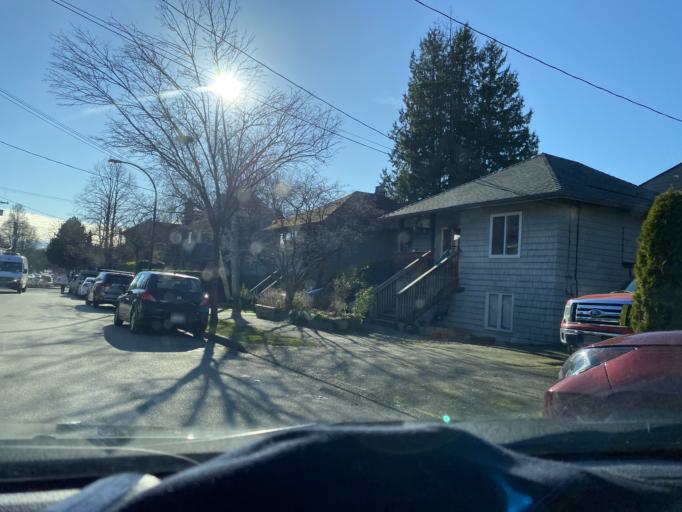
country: CA
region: British Columbia
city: West End
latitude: 49.2656
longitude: -123.1577
